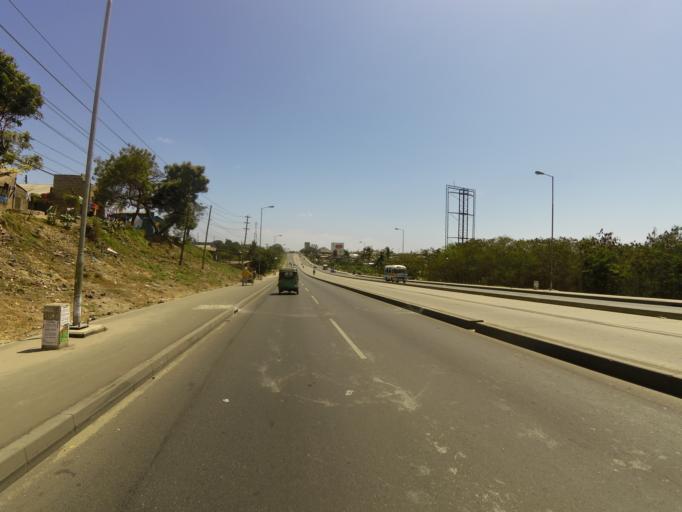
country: TZ
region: Dar es Salaam
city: Magomeni
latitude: -6.8027
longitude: 39.2616
